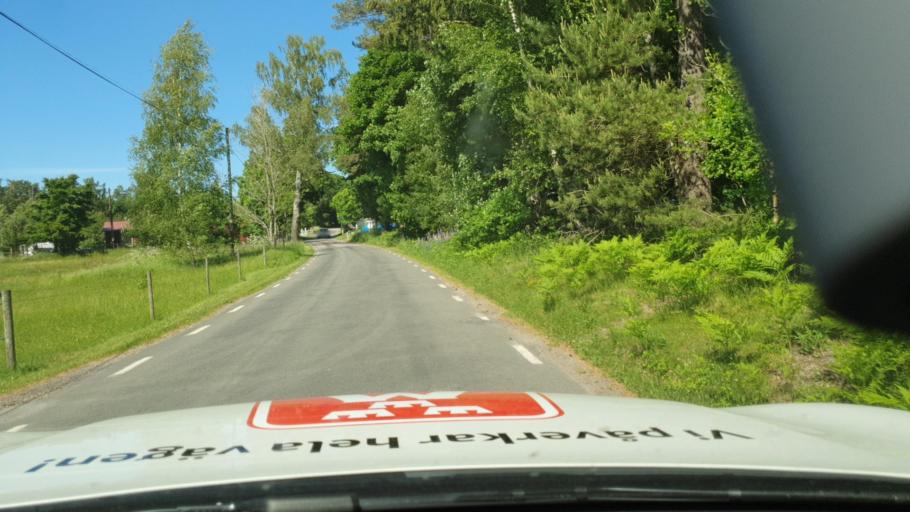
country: SE
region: Vaestra Goetaland
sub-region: Skovde Kommun
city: Skultorp
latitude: 58.2972
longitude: 13.8330
